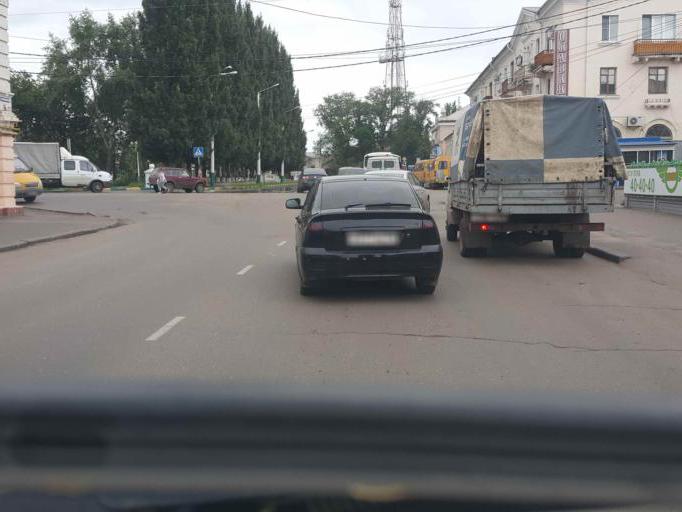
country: RU
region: Tambov
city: Michurinsk
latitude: 52.8937
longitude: 40.5000
